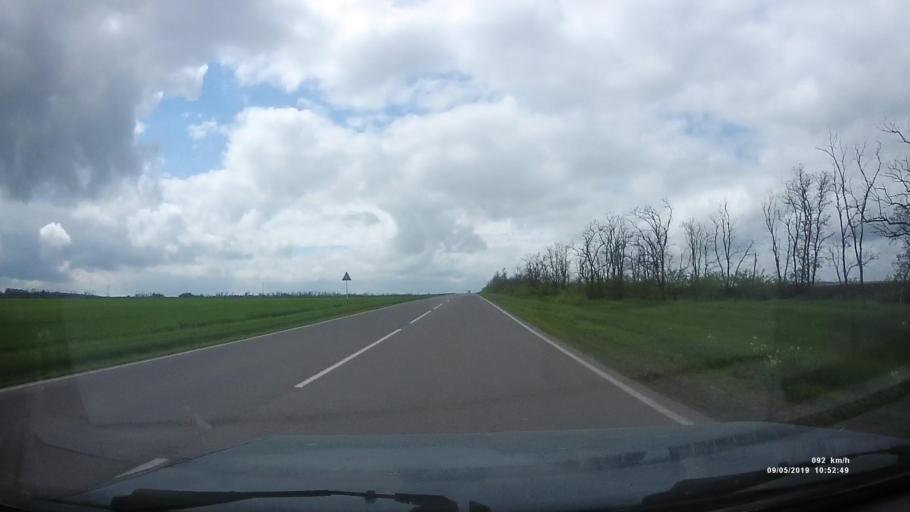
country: RU
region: Rostov
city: Peshkovo
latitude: 46.8962
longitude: 39.3489
